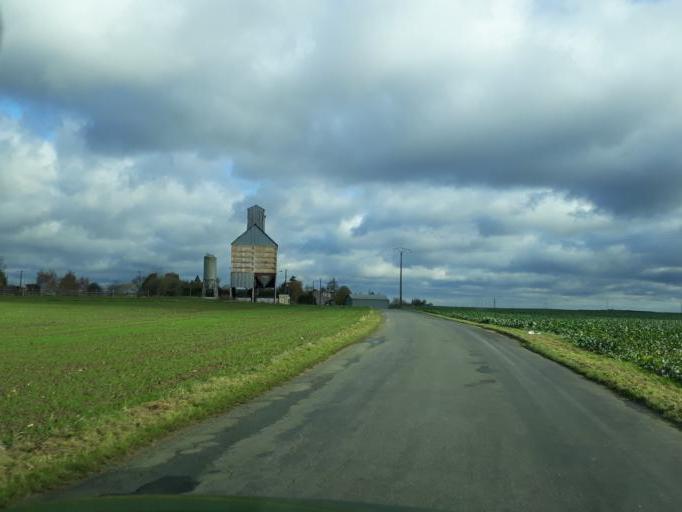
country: FR
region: Centre
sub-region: Departement du Loiret
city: Tavers
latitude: 47.8026
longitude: 1.5421
